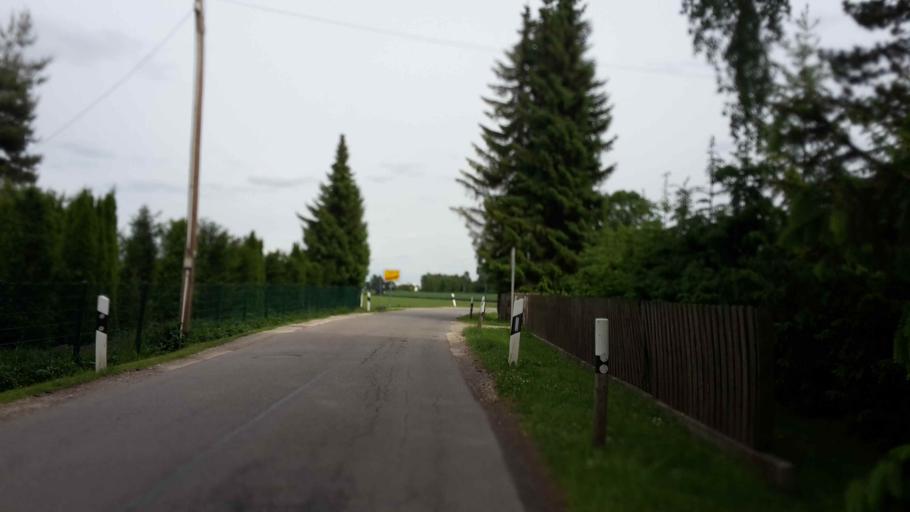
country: DE
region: Bavaria
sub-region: Upper Bavaria
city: Karlsfeld
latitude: 48.2187
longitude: 11.4274
